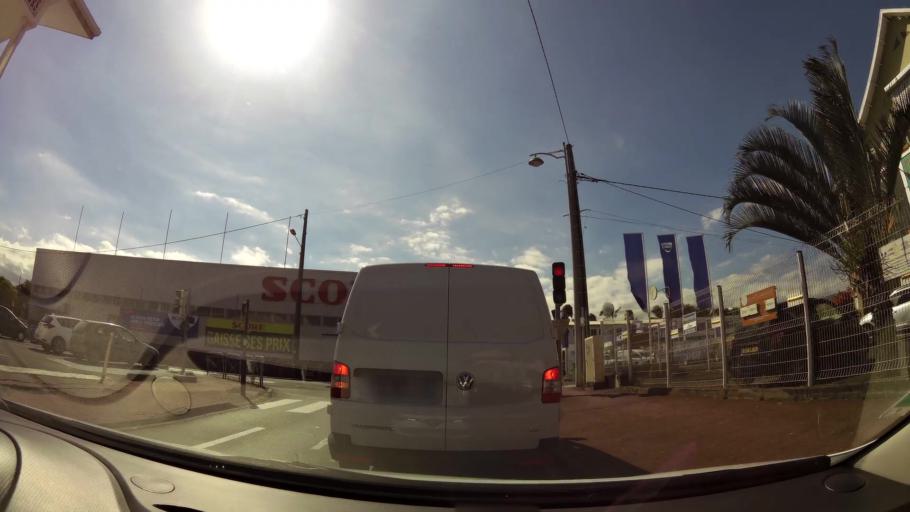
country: RE
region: Reunion
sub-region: Reunion
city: Saint-Pierre
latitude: -21.3360
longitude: 55.4680
